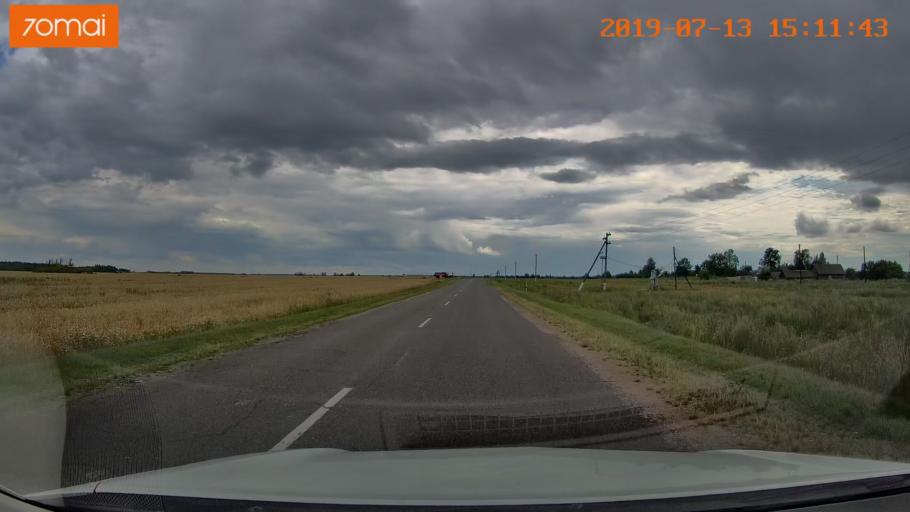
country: BY
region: Mogilev
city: Hlusha
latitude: 53.1578
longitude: 28.7869
